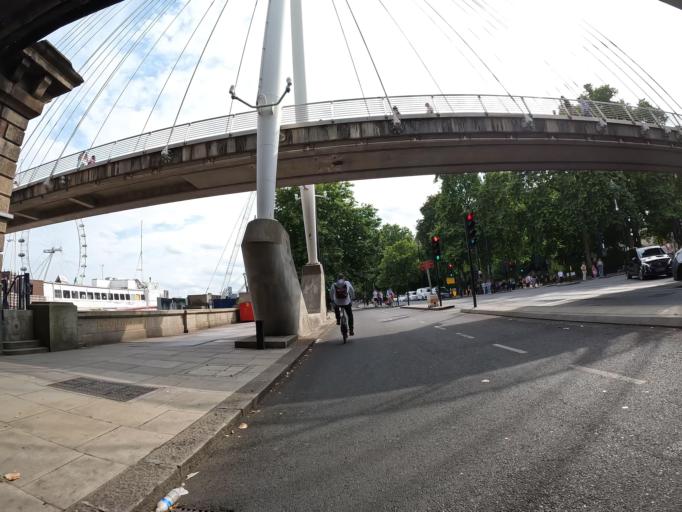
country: GB
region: England
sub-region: Greater London
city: Catford
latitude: 51.4638
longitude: -0.0193
